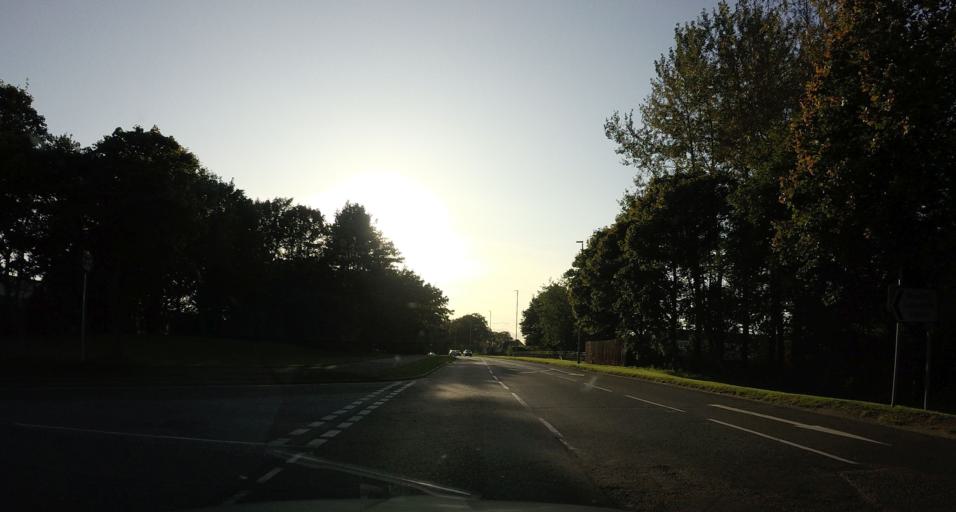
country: GB
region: Scotland
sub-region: Aberdeenshire
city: Westhill
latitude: 57.1502
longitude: -2.2815
